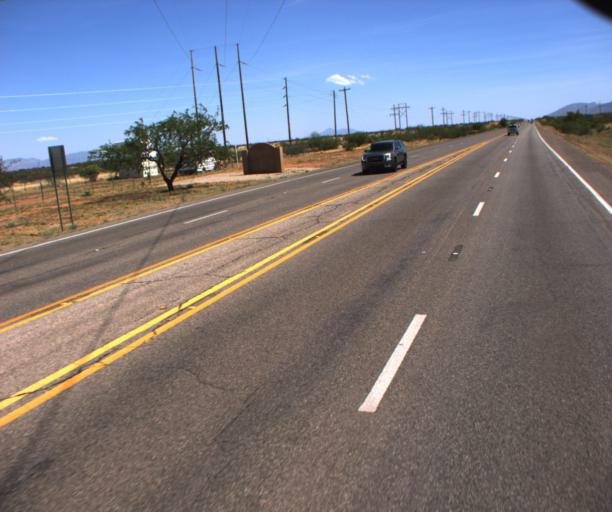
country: US
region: Arizona
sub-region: Cochise County
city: Huachuca City
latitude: 31.6162
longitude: -110.3347
